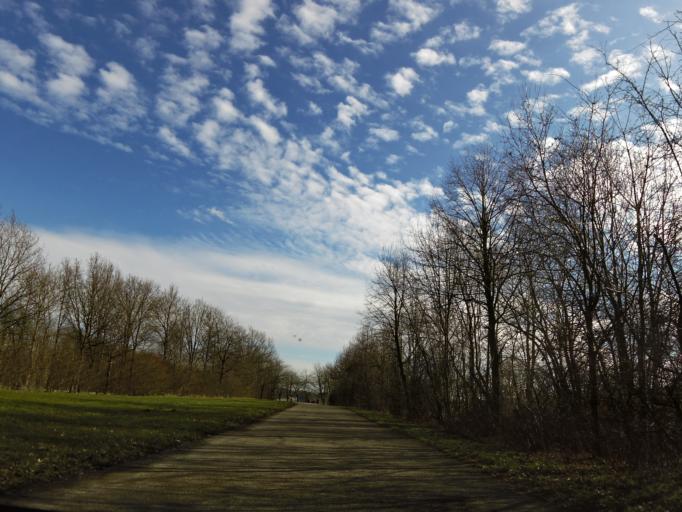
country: NL
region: Limburg
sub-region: Gemeente Simpelveld
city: Simpelveld
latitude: 50.8468
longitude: 5.9838
